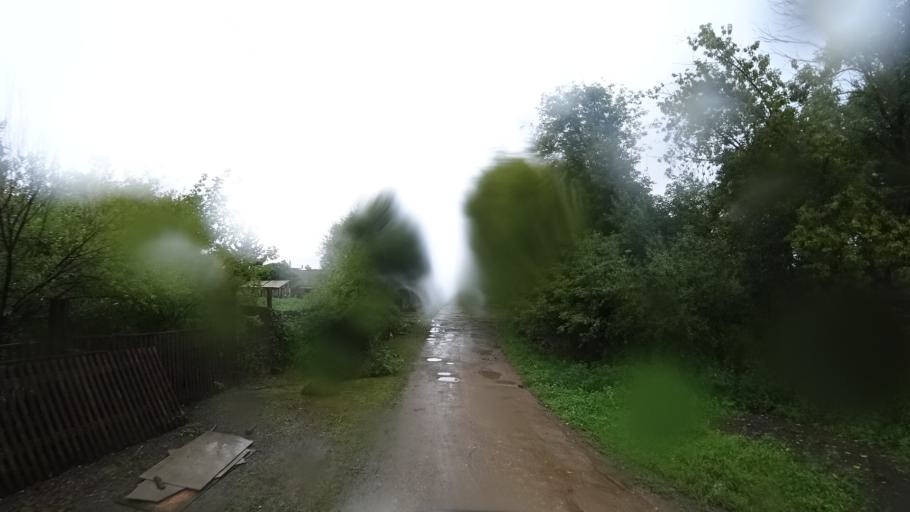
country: RU
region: Primorskiy
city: Monastyrishche
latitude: 44.2575
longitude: 132.4278
